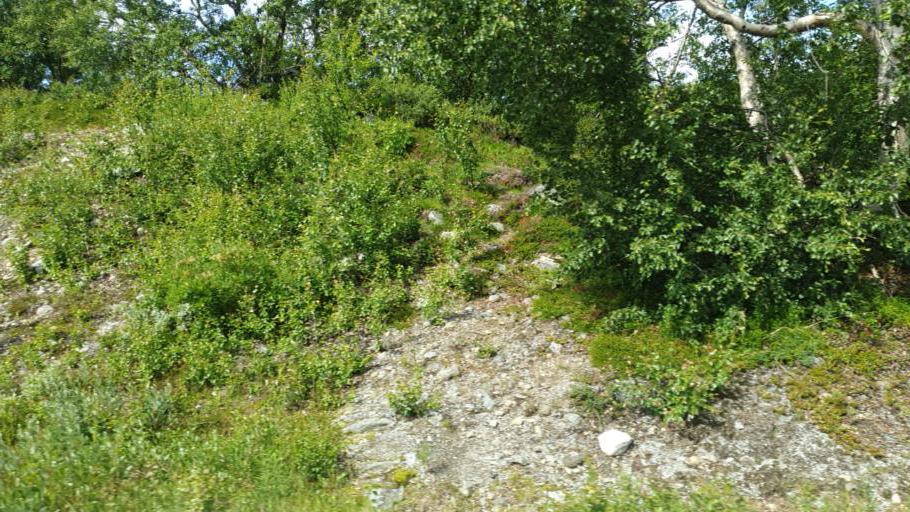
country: NO
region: Oppland
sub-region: Oystre Slidre
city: Heggenes
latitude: 61.4898
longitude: 8.8400
